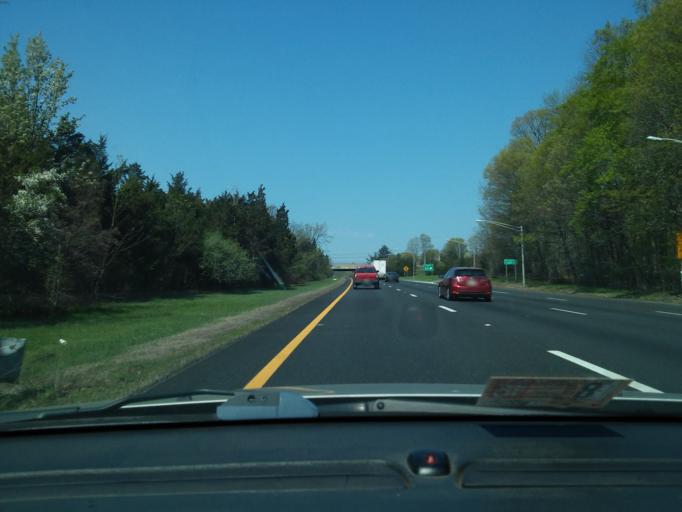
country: US
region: New Jersey
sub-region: Somerset County
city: Martinsville
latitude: 40.6468
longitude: -74.5714
